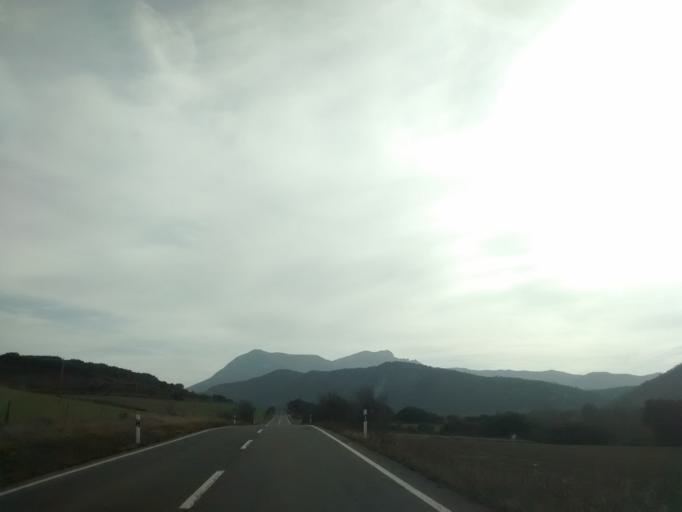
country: ES
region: Aragon
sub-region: Provincia de Huesca
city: Bailo
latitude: 42.5676
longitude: -0.8068
